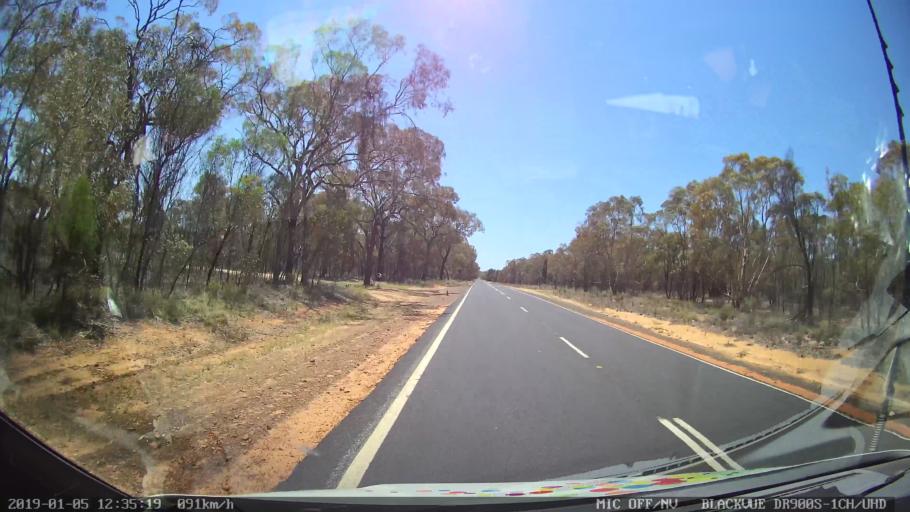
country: AU
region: New South Wales
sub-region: Warrumbungle Shire
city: Coonabarabran
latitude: -31.2099
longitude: 149.4237
